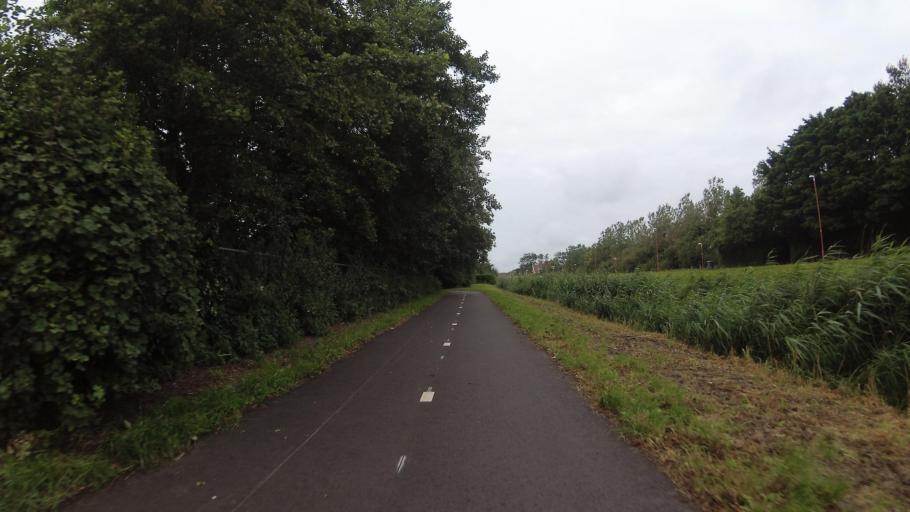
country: NL
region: North Holland
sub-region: Gemeente Den Helder
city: Den Helder
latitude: 52.8997
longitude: 4.7307
